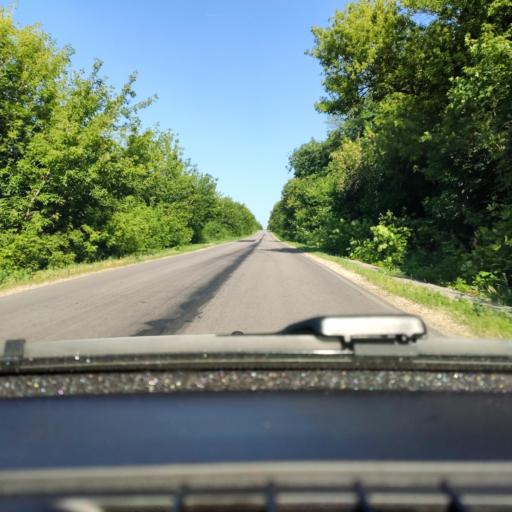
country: RU
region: Voronezj
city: Pereleshinskiy
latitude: 51.6184
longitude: 40.2424
